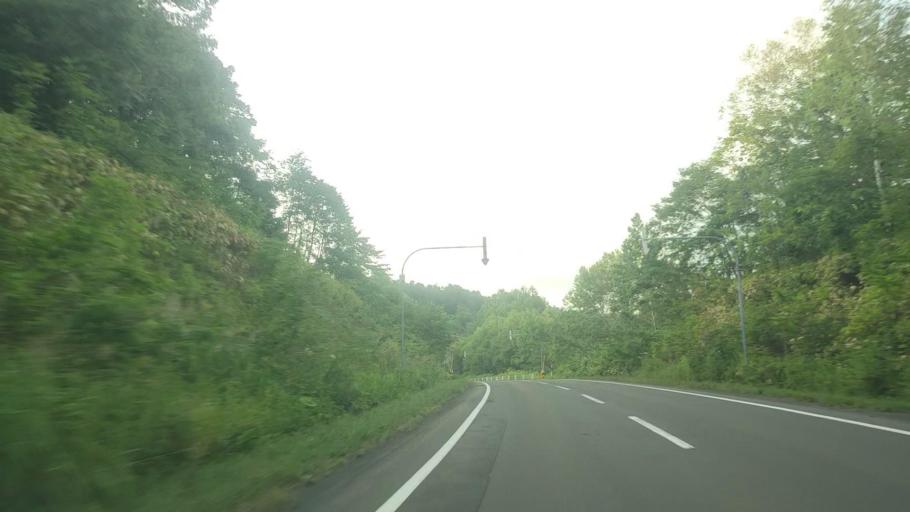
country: JP
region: Hokkaido
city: Bibai
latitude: 43.1136
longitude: 142.0997
